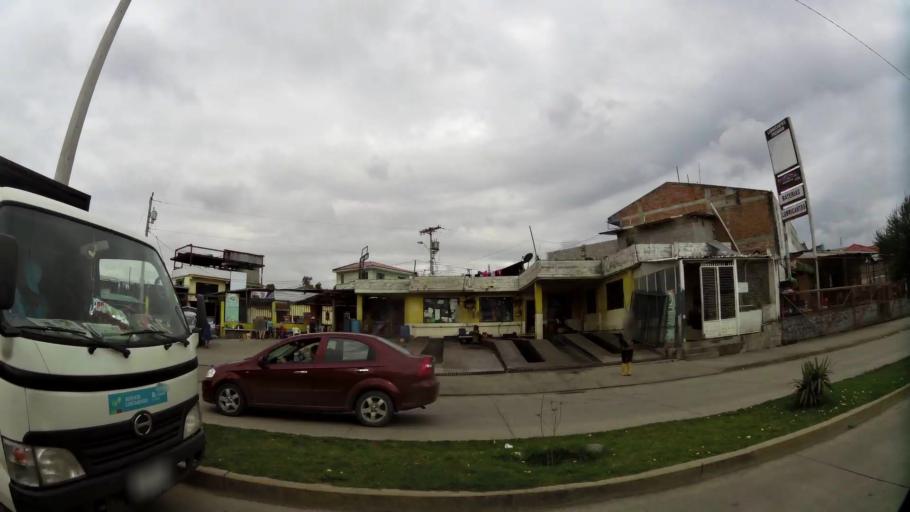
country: EC
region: Azuay
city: Cuenca
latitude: -2.8997
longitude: -78.9770
